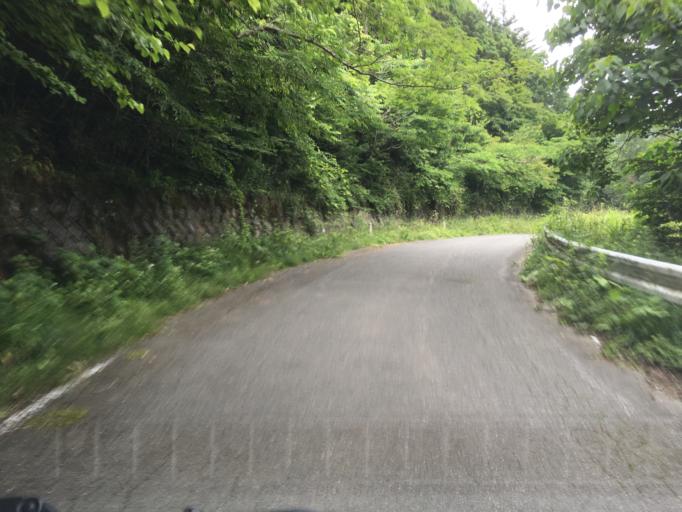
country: JP
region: Miyagi
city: Marumori
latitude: 37.7741
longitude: 140.8315
